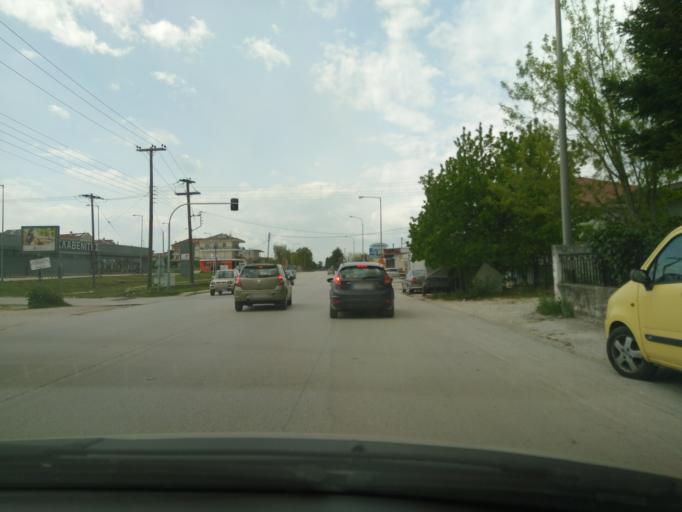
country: GR
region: Epirus
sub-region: Nomos Ioanninon
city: Eksochi
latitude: 39.6852
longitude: 20.8328
